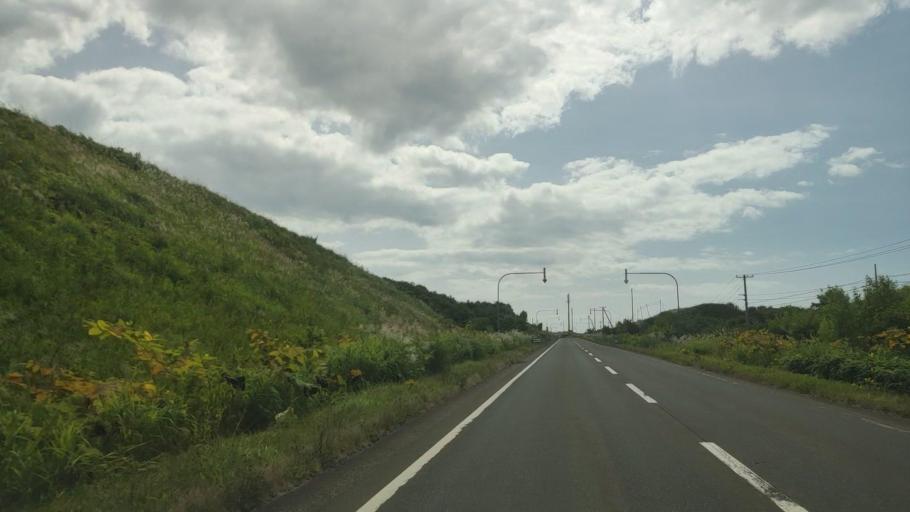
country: JP
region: Hokkaido
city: Rumoi
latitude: 44.6041
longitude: 141.7946
